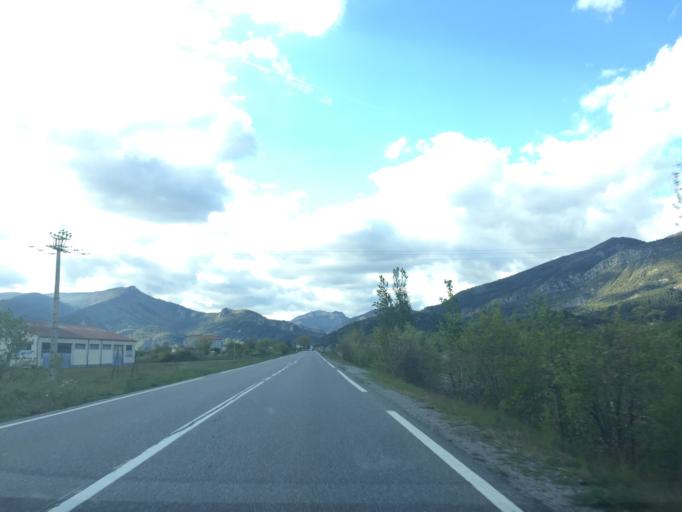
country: FR
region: Provence-Alpes-Cote d'Azur
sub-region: Departement des Hautes-Alpes
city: Serres
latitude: 44.3977
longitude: 5.7358
